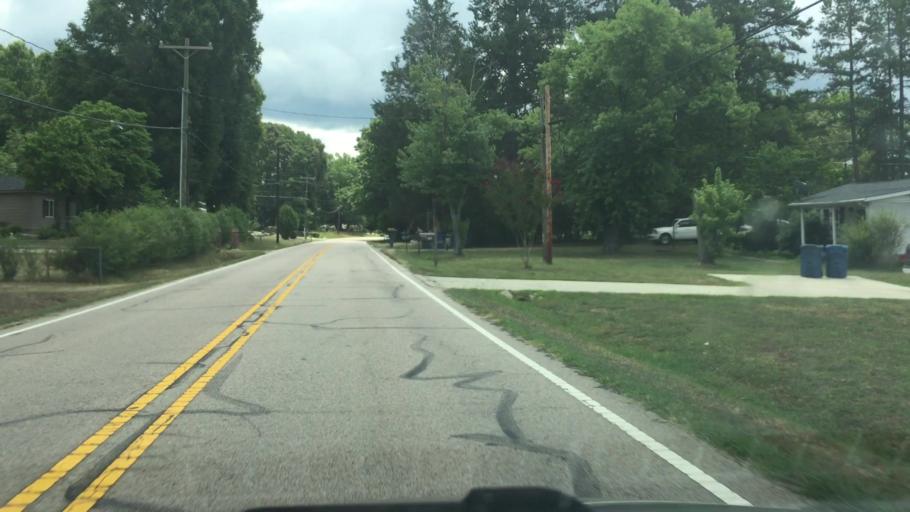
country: US
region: North Carolina
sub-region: Rowan County
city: Enochville
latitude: 35.5016
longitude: -80.6682
